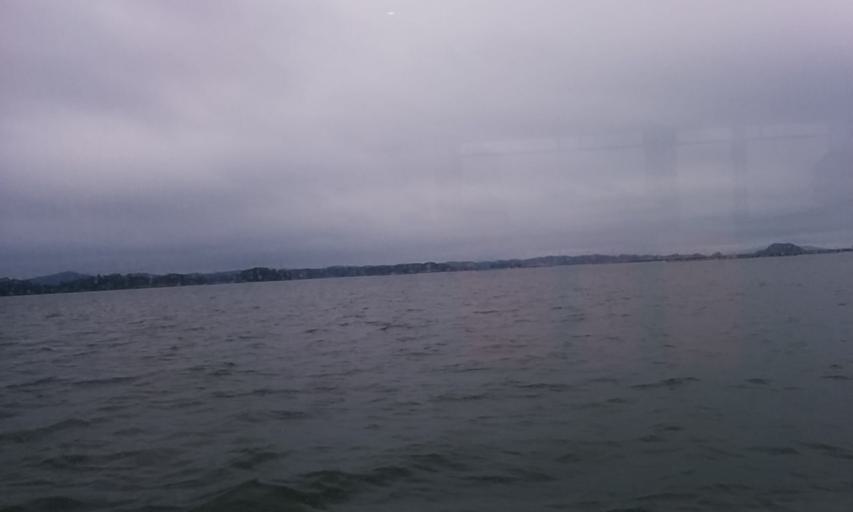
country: JP
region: Miyagi
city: Matsushima
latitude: 38.3529
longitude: 141.0764
